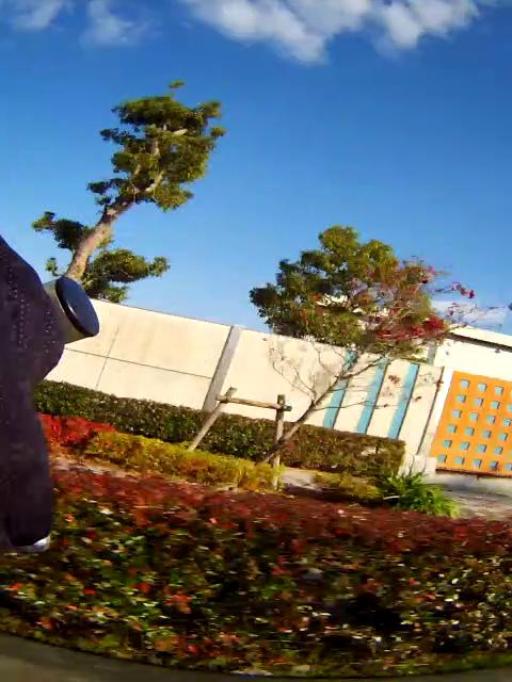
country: JP
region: Hyogo
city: Takarazuka
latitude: 34.7809
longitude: 135.3578
